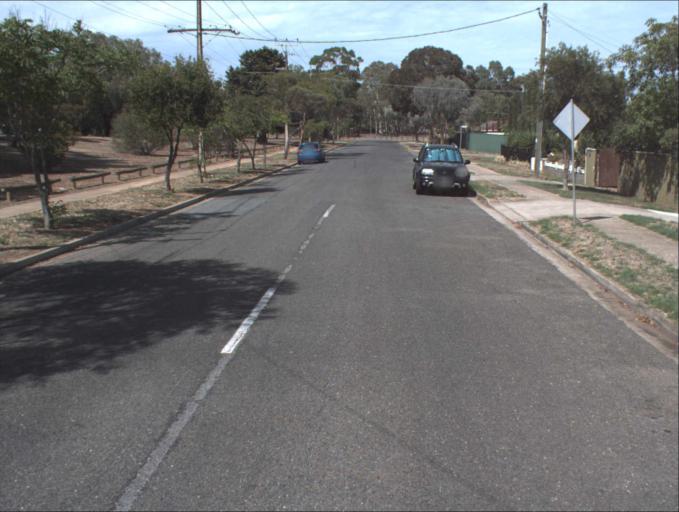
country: AU
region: South Australia
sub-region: Salisbury
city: Ingle Farm
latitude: -34.8436
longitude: 138.6264
